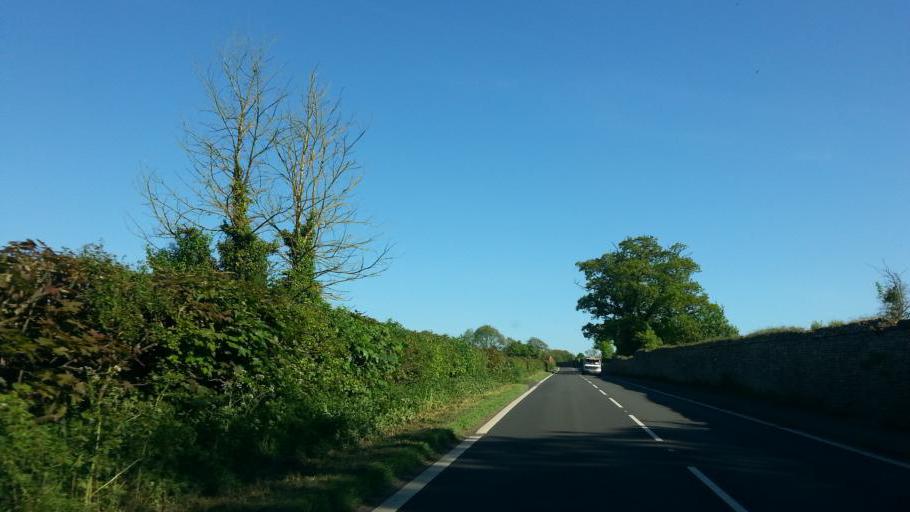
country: GB
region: England
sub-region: Dorset
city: Stalbridge
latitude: 50.9665
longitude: -2.3852
